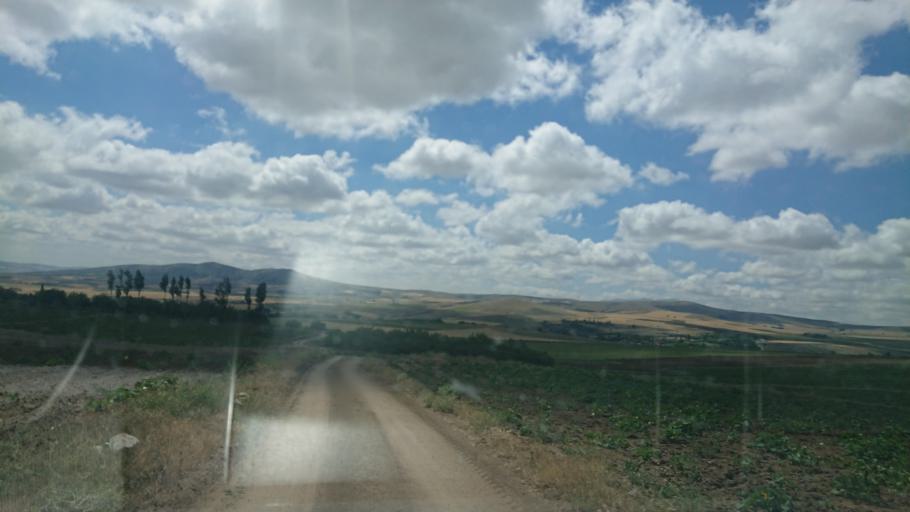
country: TR
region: Aksaray
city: Agacoren
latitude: 38.8328
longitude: 33.9489
